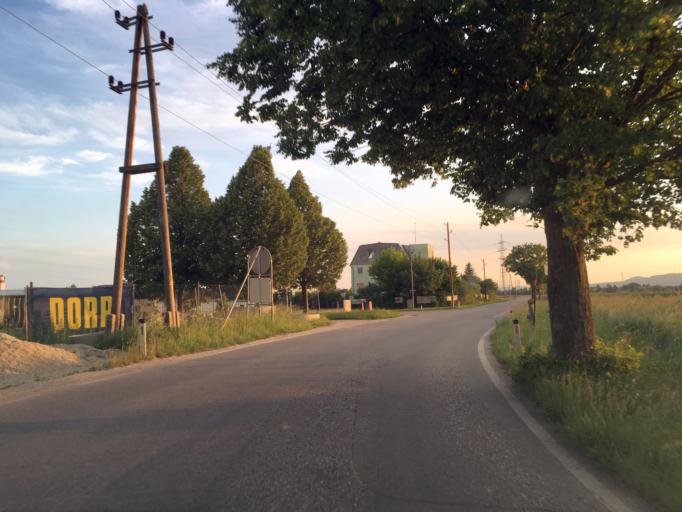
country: AT
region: Lower Austria
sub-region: Politischer Bezirk Wien-Umgebung
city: Gerasdorf bei Wien
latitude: 48.3034
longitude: 16.4844
